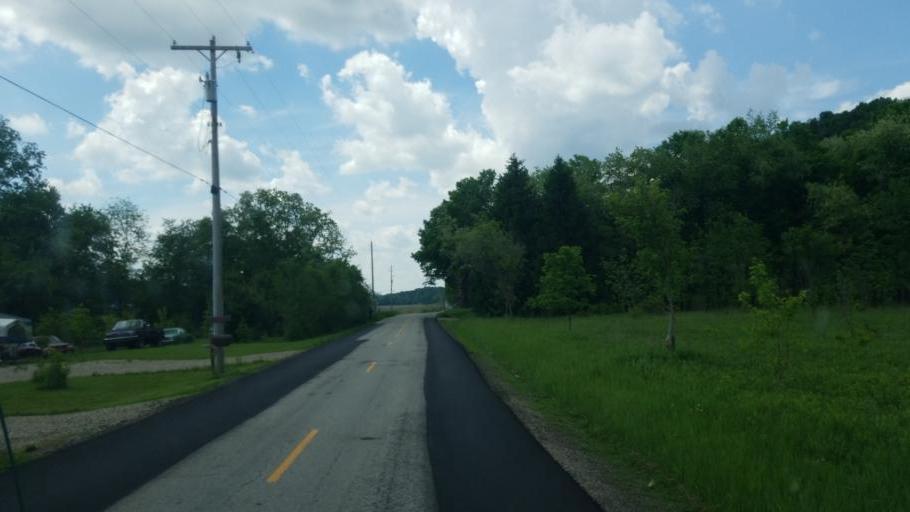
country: US
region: Ohio
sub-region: Sandusky County
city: Bellville
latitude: 40.6693
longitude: -82.4302
